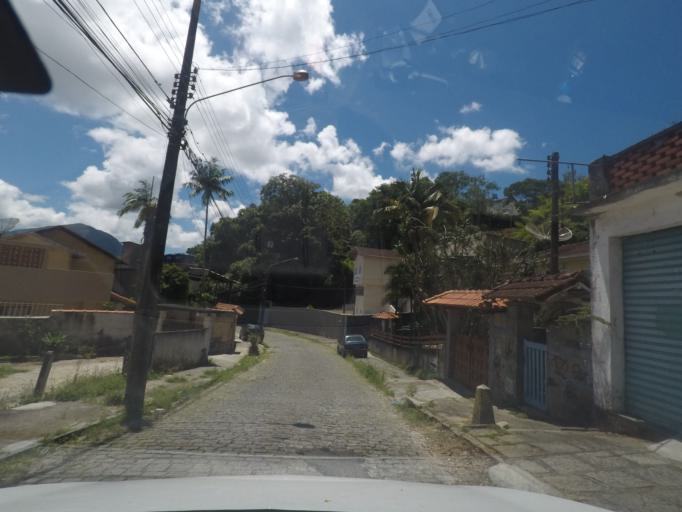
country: BR
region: Rio de Janeiro
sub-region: Teresopolis
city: Teresopolis
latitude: -22.4224
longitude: -42.9830
